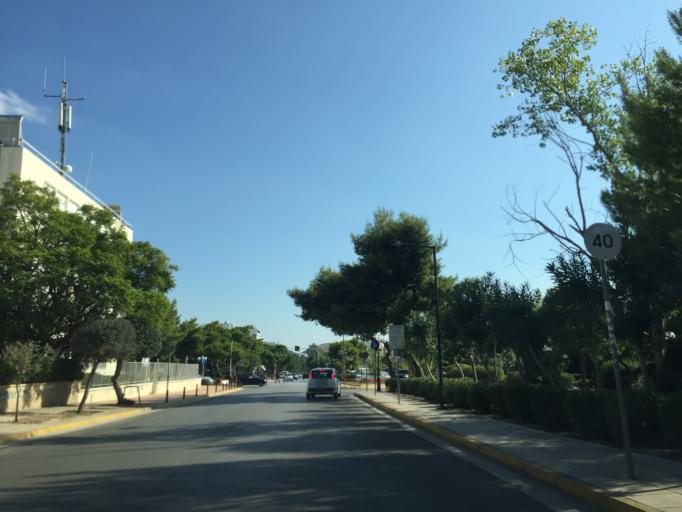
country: GR
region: Attica
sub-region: Nomarchia Anatolikis Attikis
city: Voula
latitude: 37.8418
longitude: 23.7647
